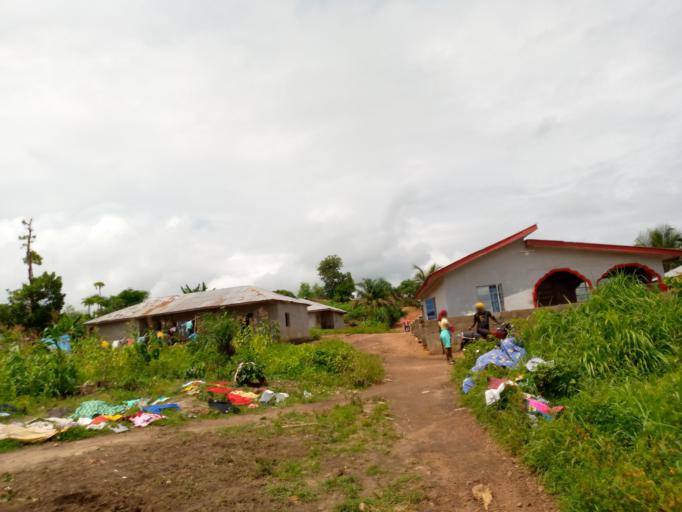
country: SL
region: Northern Province
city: Magburaka
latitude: 8.7283
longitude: -11.9349
